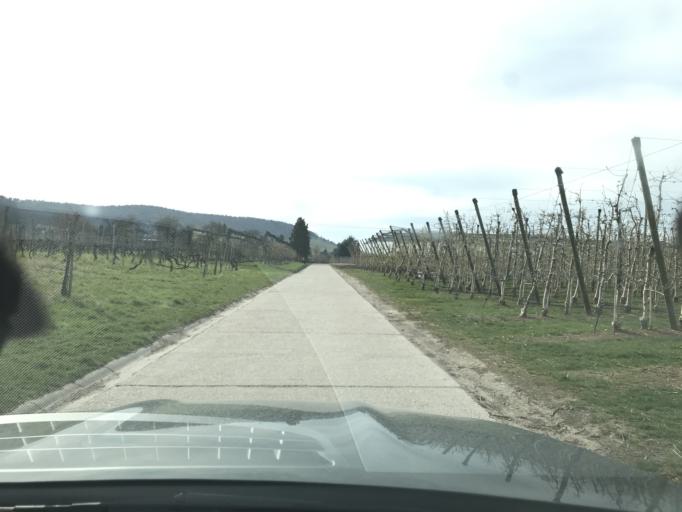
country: DE
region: Baden-Wuerttemberg
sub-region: Regierungsbezirk Stuttgart
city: Waiblingen
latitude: 48.7940
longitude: 9.3282
